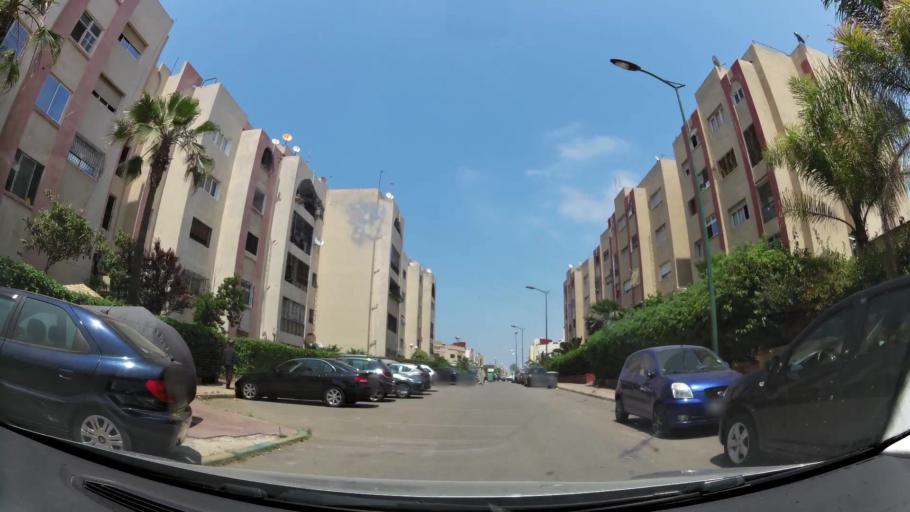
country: MA
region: Rabat-Sale-Zemmour-Zaer
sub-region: Skhirate-Temara
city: Temara
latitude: 33.9750
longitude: -6.8955
